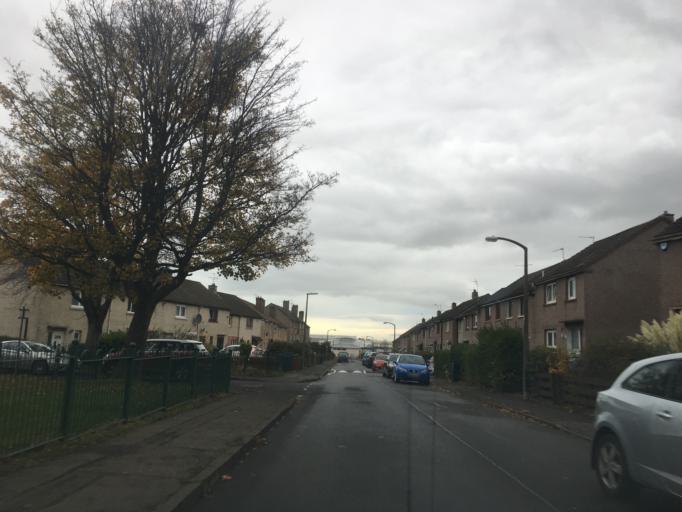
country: GB
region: Scotland
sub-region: Midlothian
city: Loanhead
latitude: 55.9018
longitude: -3.1594
